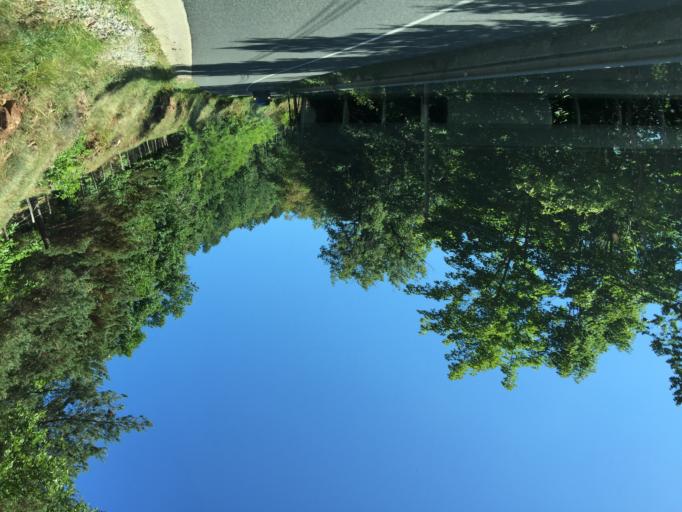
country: FR
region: Midi-Pyrenees
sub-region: Departement de l'Aveyron
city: Saint-Georges-de-Luzencon
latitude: 44.0996
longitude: 2.9006
